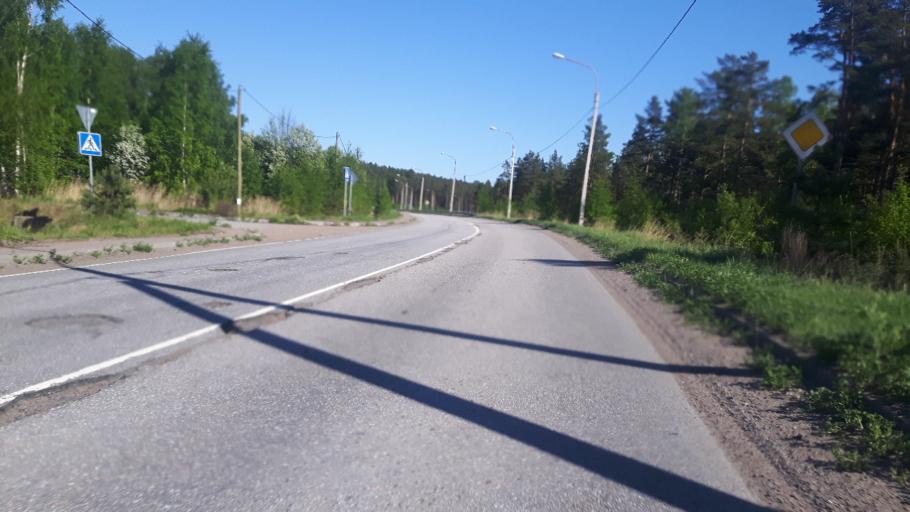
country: RU
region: Leningrad
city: Sosnovyy Bor
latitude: 60.1902
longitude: 29.0159
